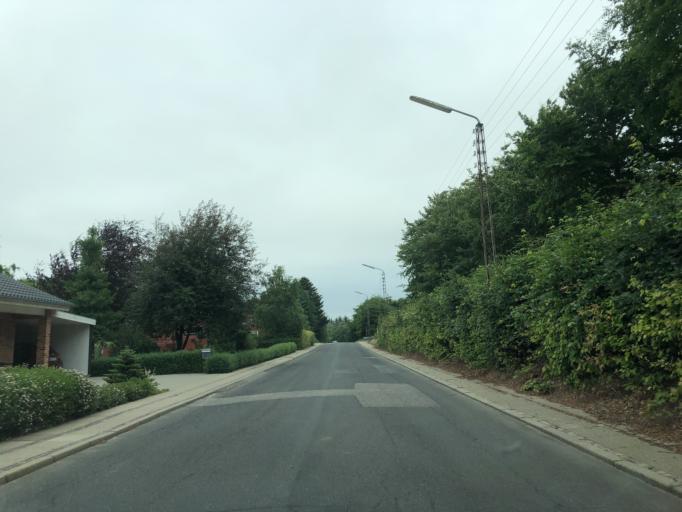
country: DK
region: Central Jutland
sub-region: Ringkobing-Skjern Kommune
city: Videbaek
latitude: 56.1999
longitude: 8.5673
